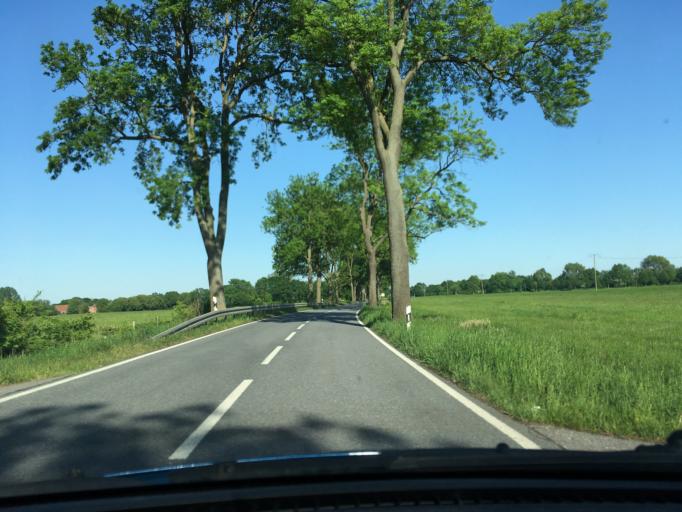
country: DE
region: Brandenburg
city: Lenzen
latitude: 53.0850
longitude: 11.4568
